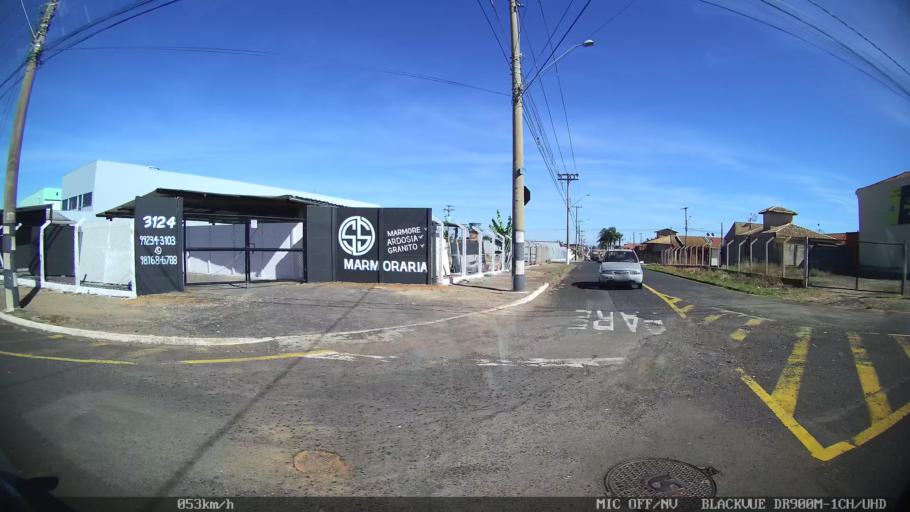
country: BR
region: Sao Paulo
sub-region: Franca
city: Franca
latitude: -20.5451
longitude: -47.3744
